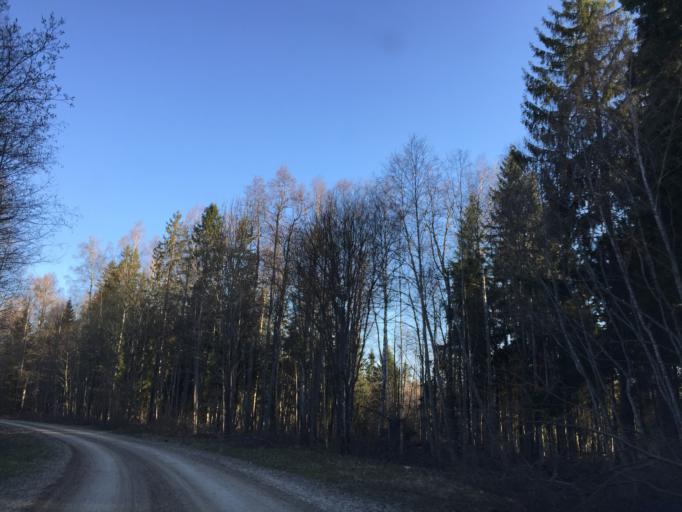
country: EE
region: Ida-Virumaa
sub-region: Sillamaee linn
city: Sillamae
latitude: 59.1493
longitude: 27.8034
